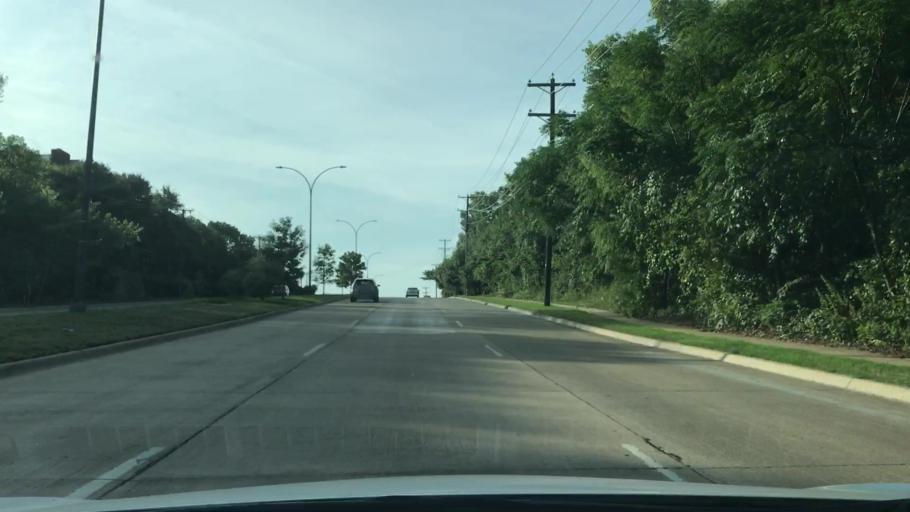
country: US
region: Texas
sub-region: Tarrant County
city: Arlington
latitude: 32.7788
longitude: -97.0849
